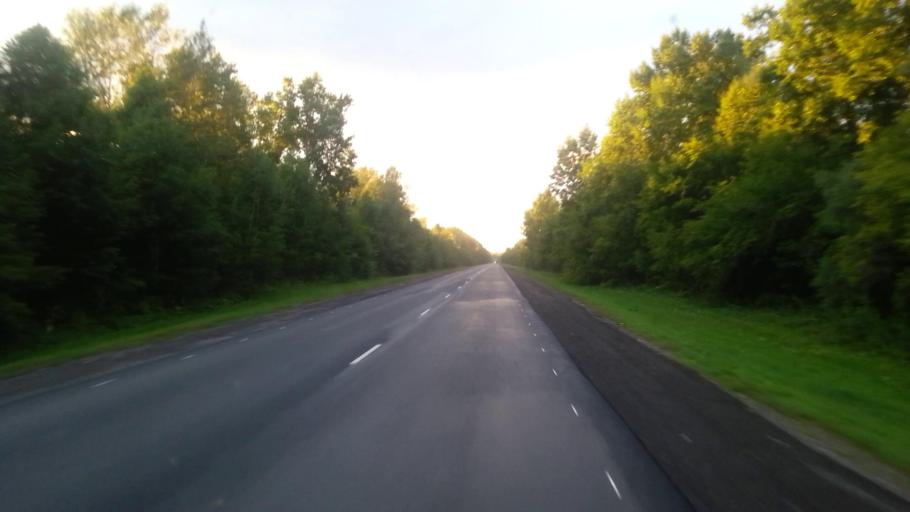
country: RU
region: Altai Krai
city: Berezovka
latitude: 52.3617
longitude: 85.8174
